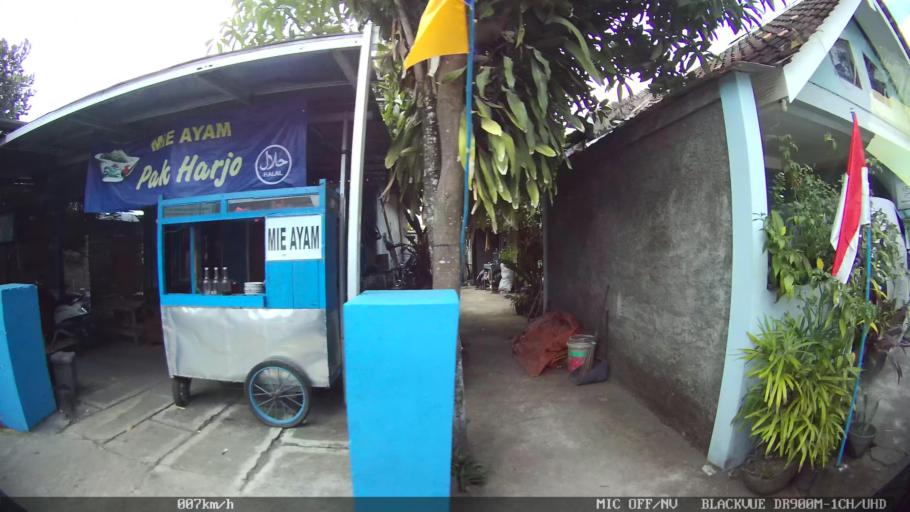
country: ID
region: Daerah Istimewa Yogyakarta
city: Kasihan
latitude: -7.8188
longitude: 110.3546
